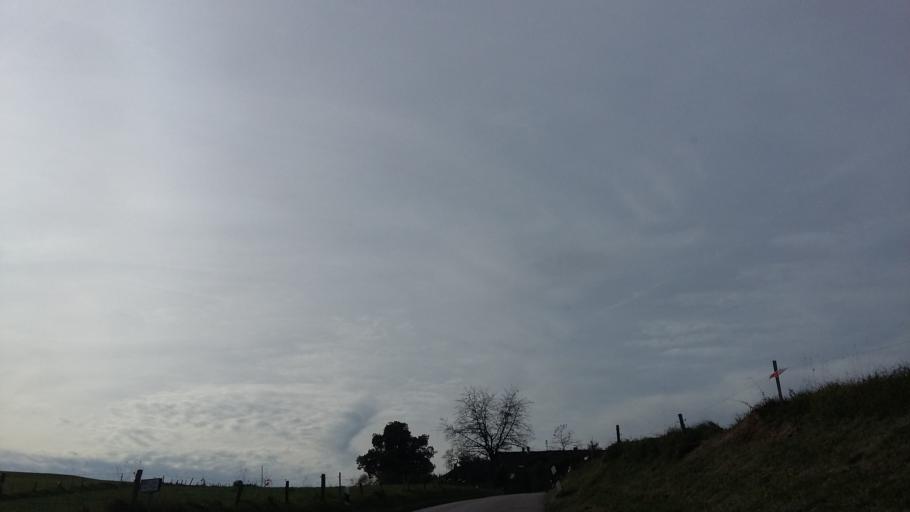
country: DE
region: Bavaria
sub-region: Upper Bavaria
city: Munsing
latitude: 47.8793
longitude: 11.3458
